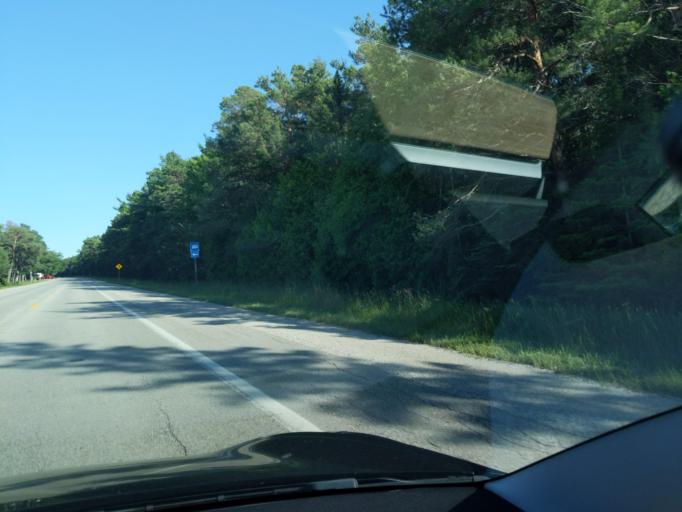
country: US
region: Michigan
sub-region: Mackinac County
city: Saint Ignace
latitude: 45.7520
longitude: -84.6897
